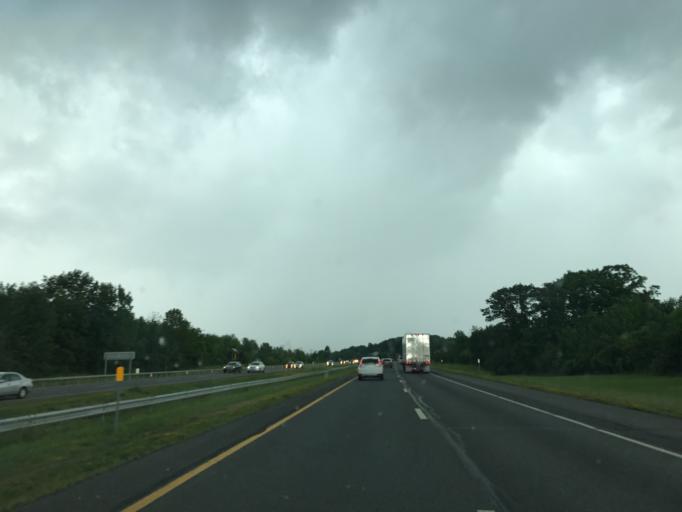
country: US
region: New York
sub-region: Albany County
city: Ravena
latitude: 42.4619
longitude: -73.8080
